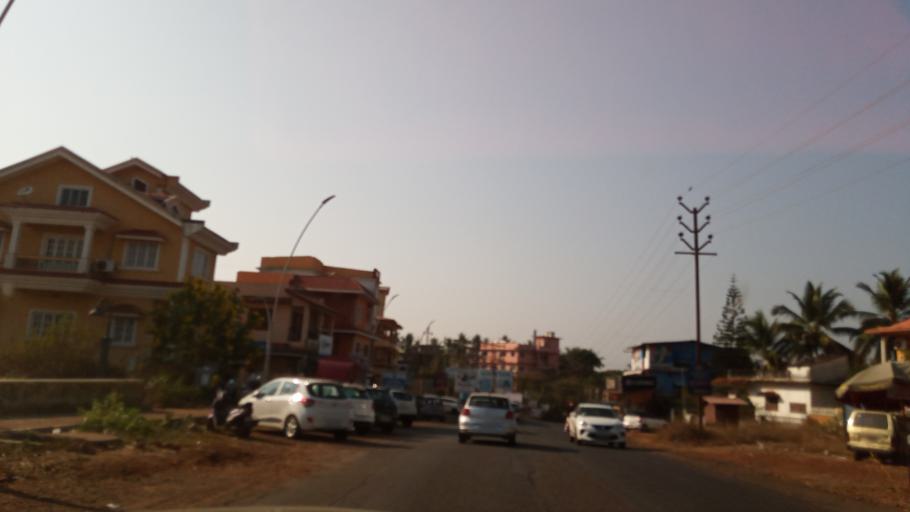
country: IN
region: Goa
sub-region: North Goa
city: Serula
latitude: 15.5393
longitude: 73.8173
